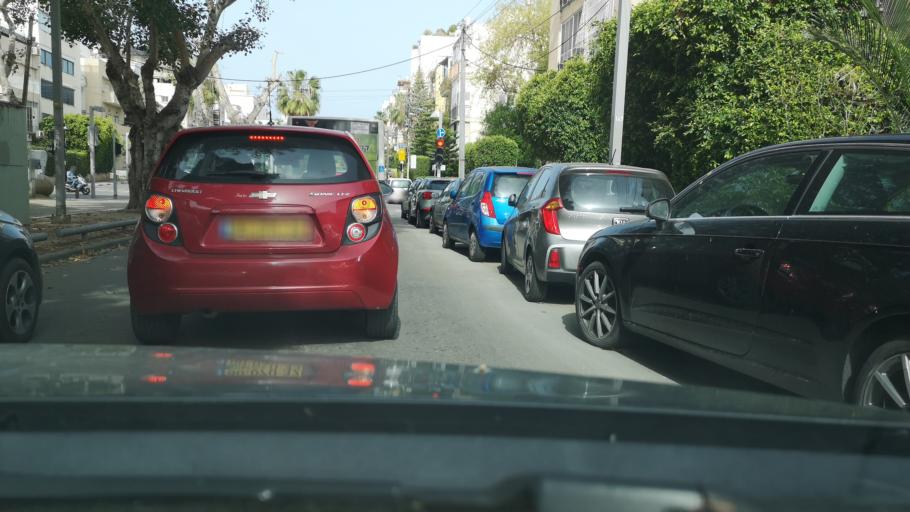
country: IL
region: Tel Aviv
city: Tel Aviv
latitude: 32.0922
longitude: 34.7788
